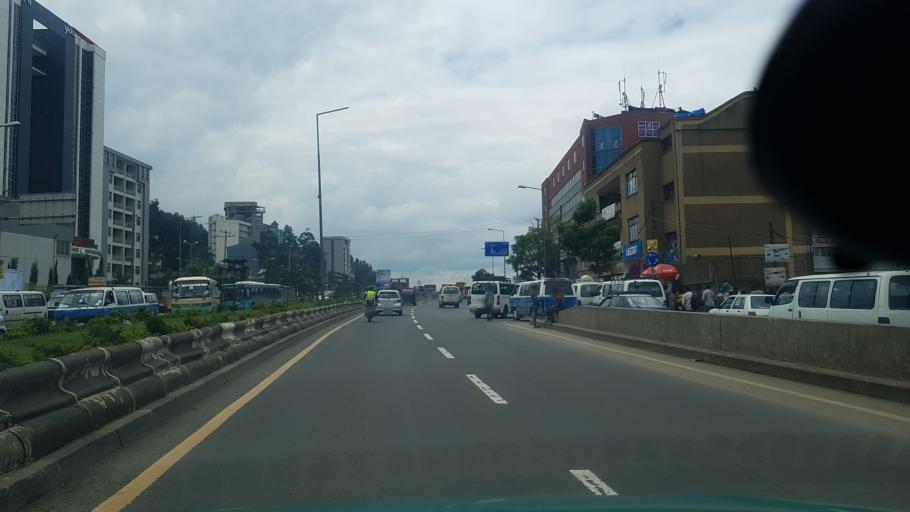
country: ET
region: Adis Abeba
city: Addis Ababa
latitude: 9.0226
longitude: 38.7994
